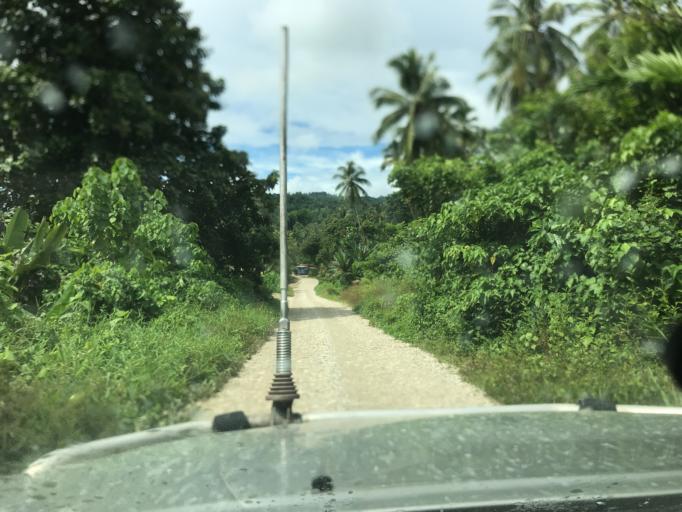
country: SB
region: Malaita
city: Auki
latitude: -8.3815
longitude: 160.6933
